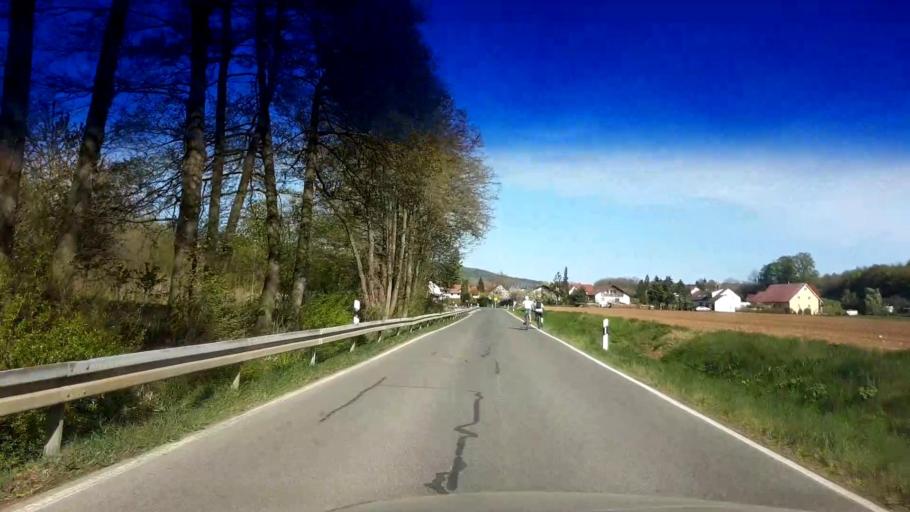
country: DE
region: Bavaria
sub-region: Upper Franconia
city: Buttenheim
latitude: 49.8069
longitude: 11.0508
